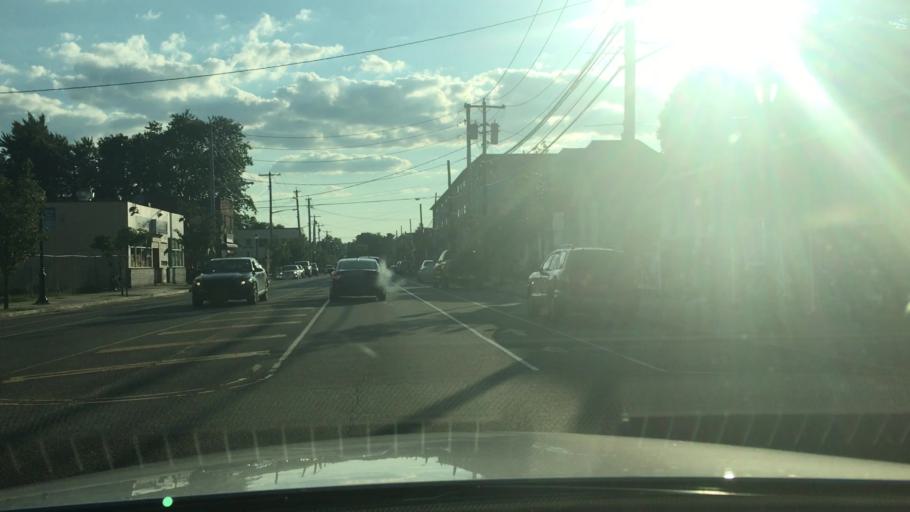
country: US
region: New York
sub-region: Nassau County
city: New Cassel
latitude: 40.7620
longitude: -73.5705
